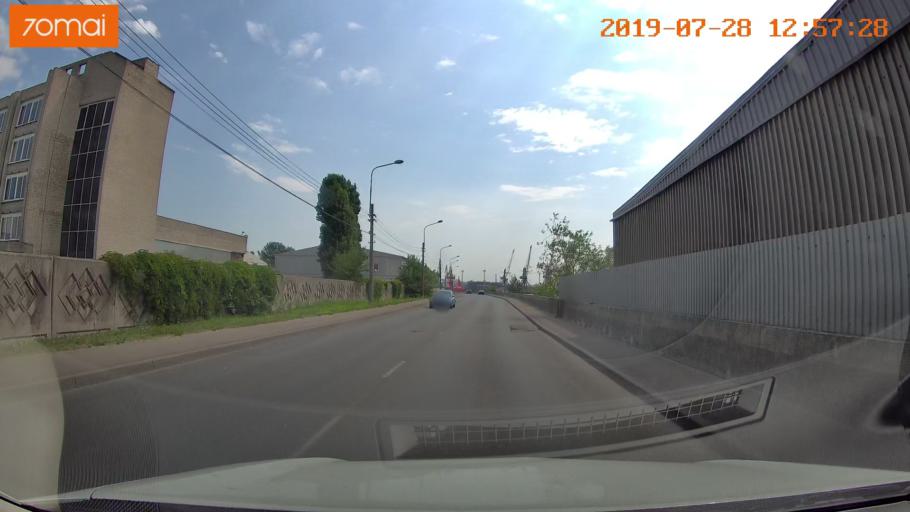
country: RU
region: Kaliningrad
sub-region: Gorod Kaliningrad
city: Kaliningrad
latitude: 54.7067
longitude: 20.4696
